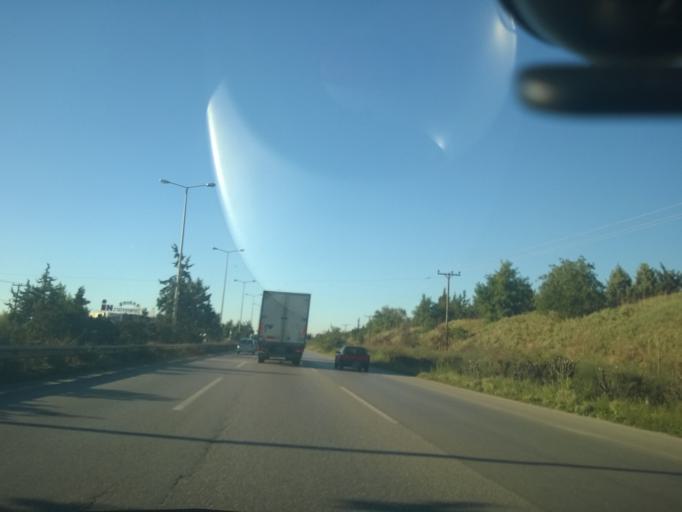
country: GR
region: Central Macedonia
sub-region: Nomos Thessalonikis
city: Thermi
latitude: 40.5645
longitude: 22.9895
